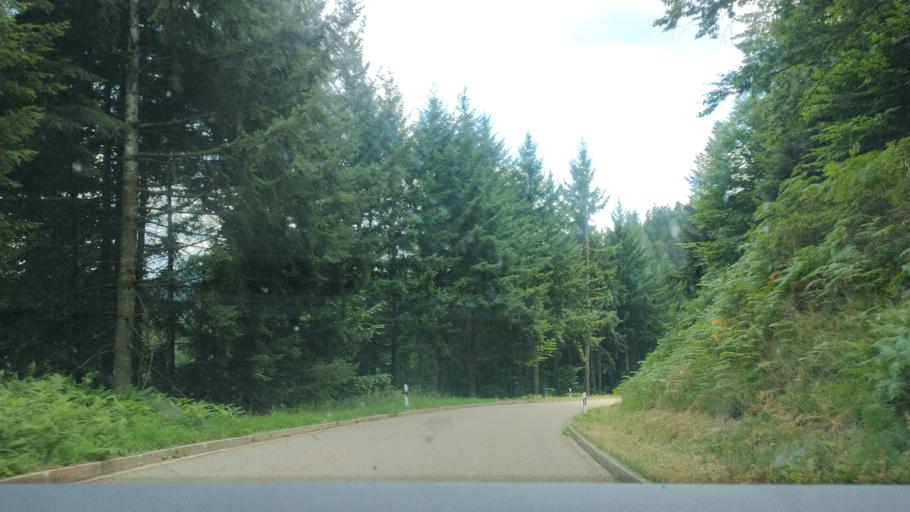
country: DE
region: Baden-Wuerttemberg
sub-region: Freiburg Region
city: Oppenau
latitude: 48.4292
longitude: 8.1556
